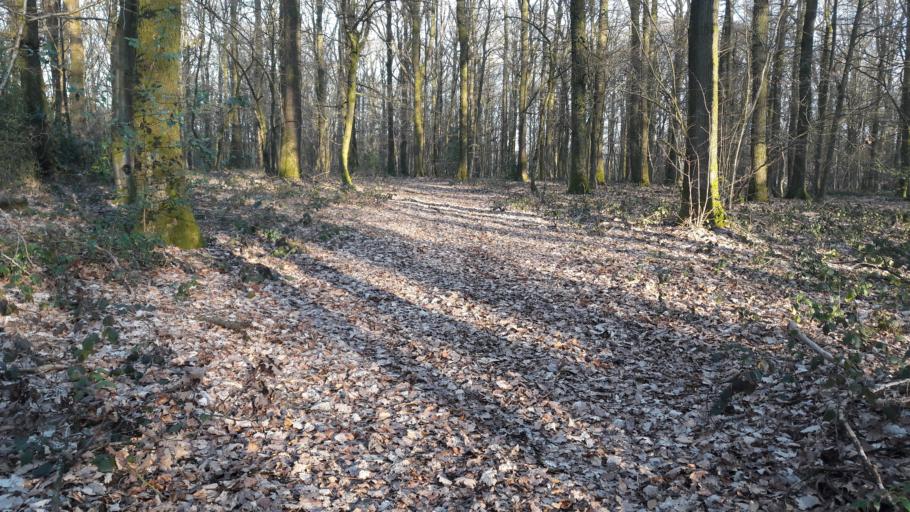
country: BE
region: Wallonia
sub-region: Province du Hainaut
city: Beaumont
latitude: 50.2443
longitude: 4.2022
